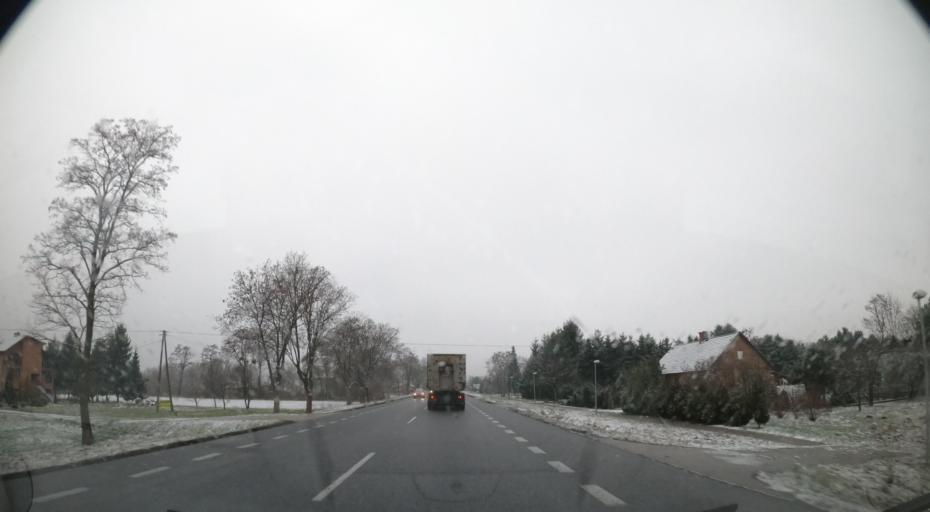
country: PL
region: Masovian Voivodeship
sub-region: Powiat sochaczewski
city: Teresin
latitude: 52.2181
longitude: 20.3632
